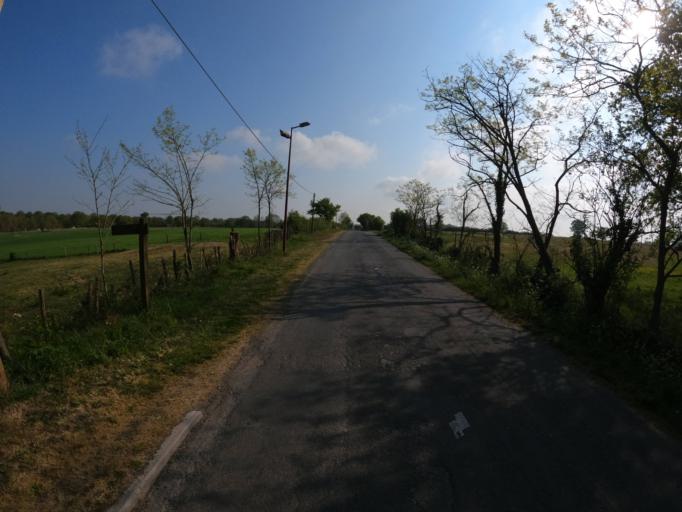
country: FR
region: Pays de la Loire
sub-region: Departement de Maine-et-Loire
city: Torfou
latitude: 47.0425
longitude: -1.1099
